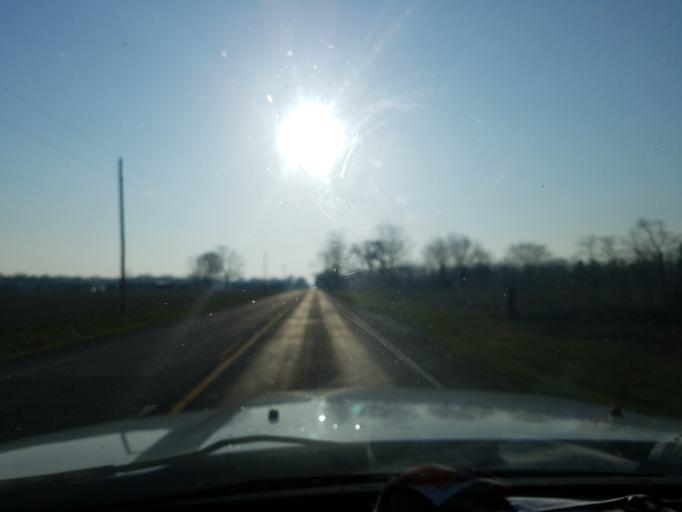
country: US
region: Indiana
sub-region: Vigo County
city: Seelyville
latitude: 39.3884
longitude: -87.1788
